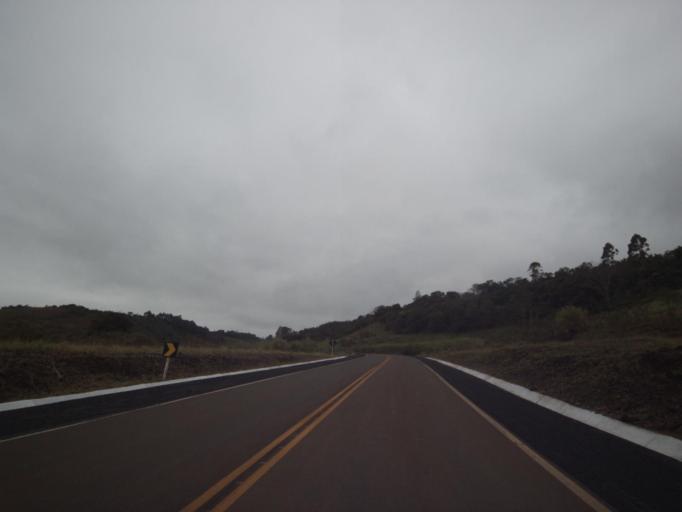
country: AR
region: Misiones
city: El Soberbio
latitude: -27.2868
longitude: -54.1843
